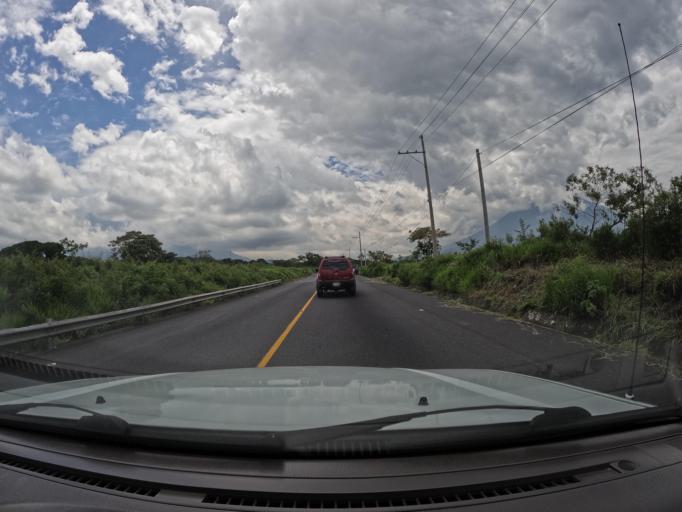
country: GT
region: Escuintla
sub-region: Municipio de Escuintla
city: Escuintla
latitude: 14.3866
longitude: -90.8266
